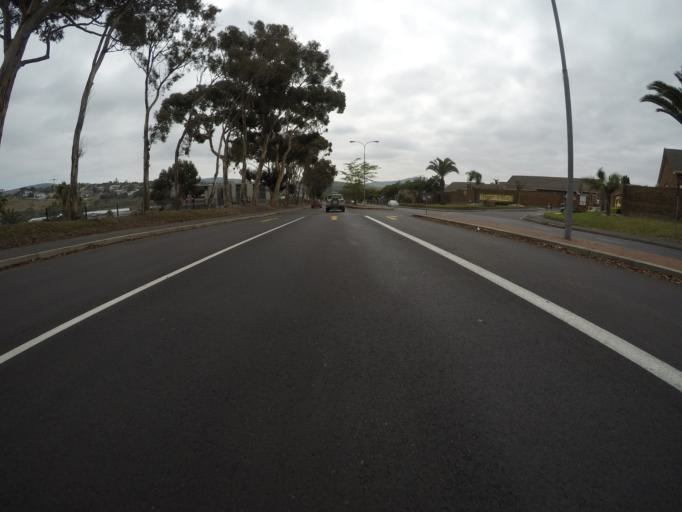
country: ZA
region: Western Cape
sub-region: City of Cape Town
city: Kraaifontein
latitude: -33.8708
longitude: 18.6357
